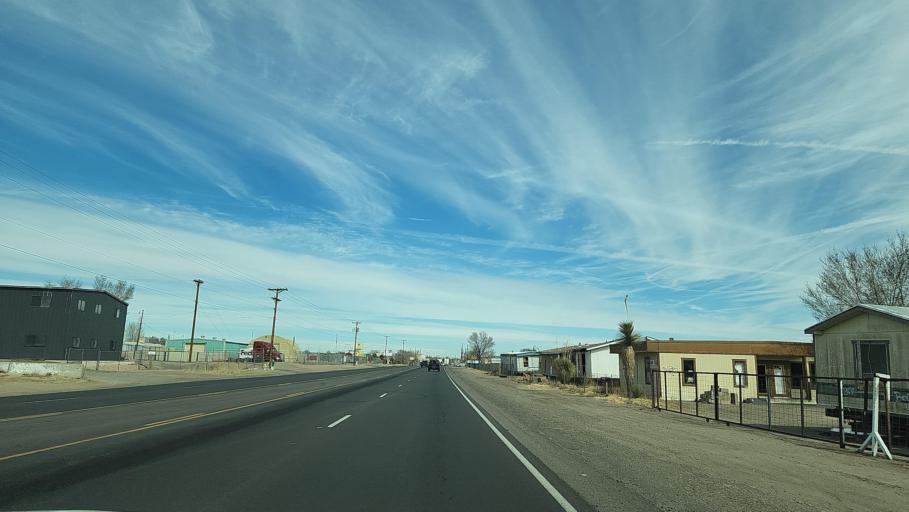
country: US
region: New Mexico
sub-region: Bernalillo County
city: South Valley
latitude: 35.0396
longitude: -106.7114
